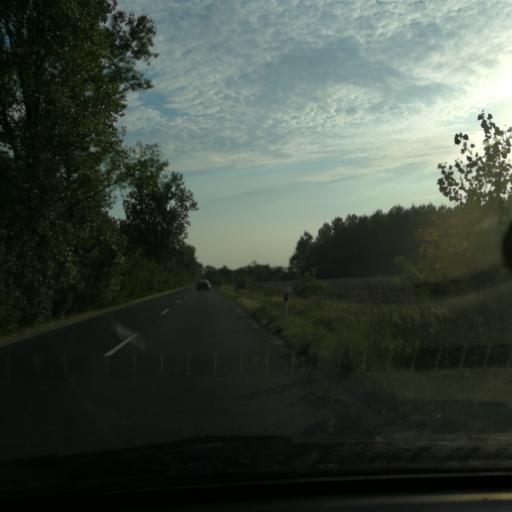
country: HU
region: Bacs-Kiskun
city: Jaszszentlaszlo
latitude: 46.5770
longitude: 19.7704
